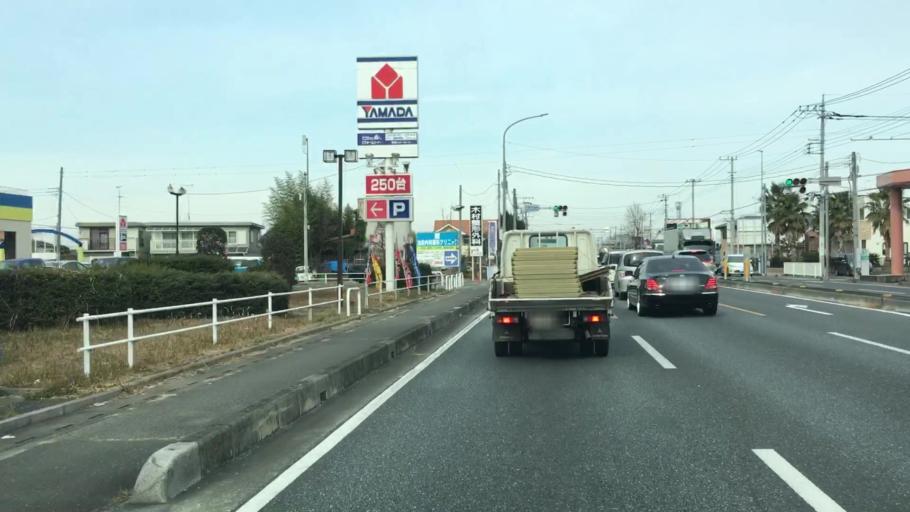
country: JP
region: Saitama
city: Kumagaya
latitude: 36.1616
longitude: 139.3708
